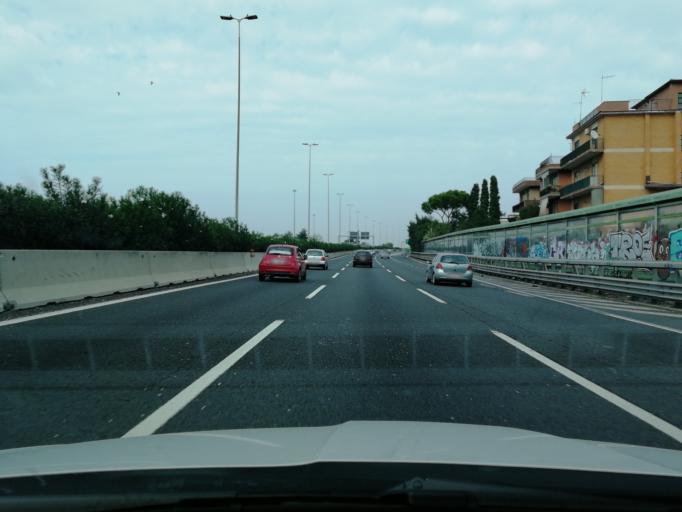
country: IT
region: Latium
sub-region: Citta metropolitana di Roma Capitale
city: Ciampino
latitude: 41.8610
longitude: 12.5998
